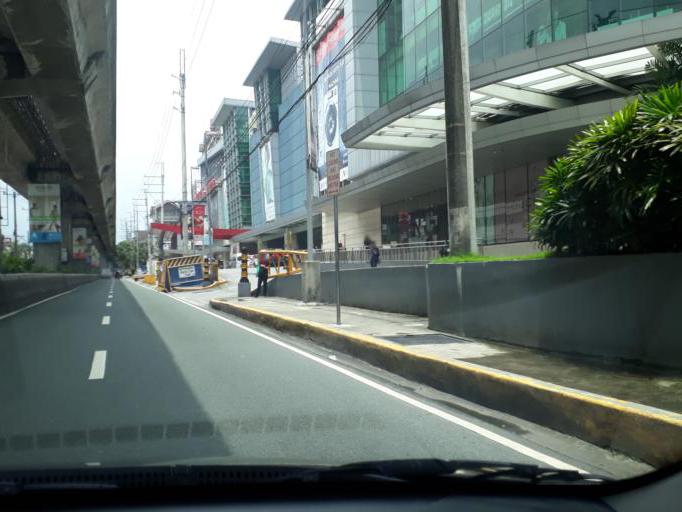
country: PH
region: Metro Manila
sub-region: San Juan
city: San Juan
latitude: 14.6152
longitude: 121.0372
